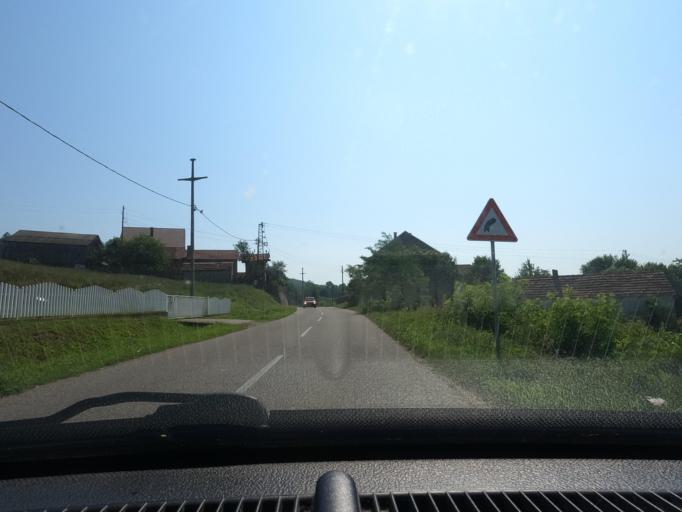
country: RS
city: Jadranska Lesnica
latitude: 44.5527
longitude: 19.3289
